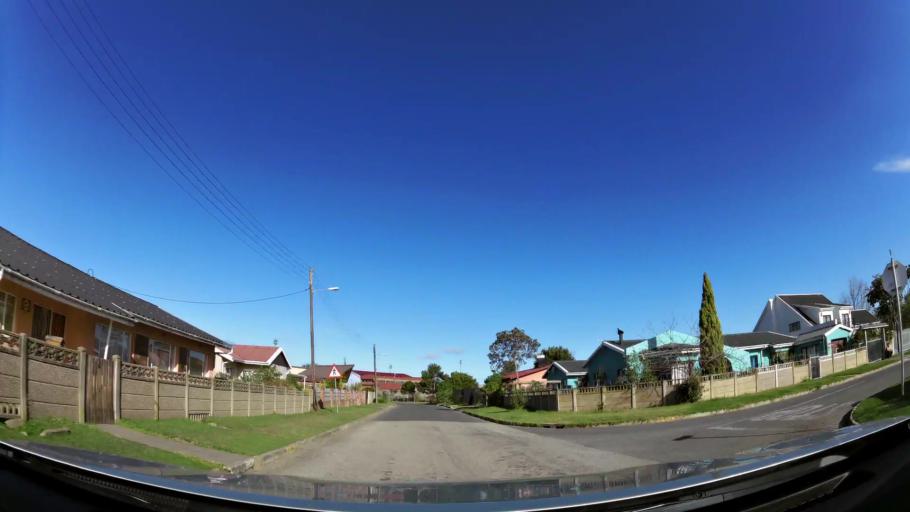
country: ZA
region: Western Cape
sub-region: Eden District Municipality
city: George
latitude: -33.9673
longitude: 22.4786
